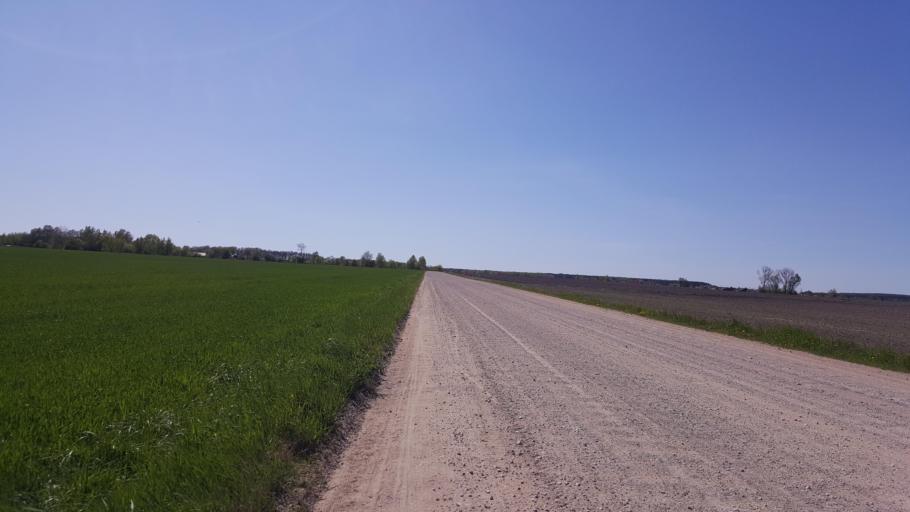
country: BY
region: Brest
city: Kamyanyets
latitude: 52.4463
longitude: 23.8568
